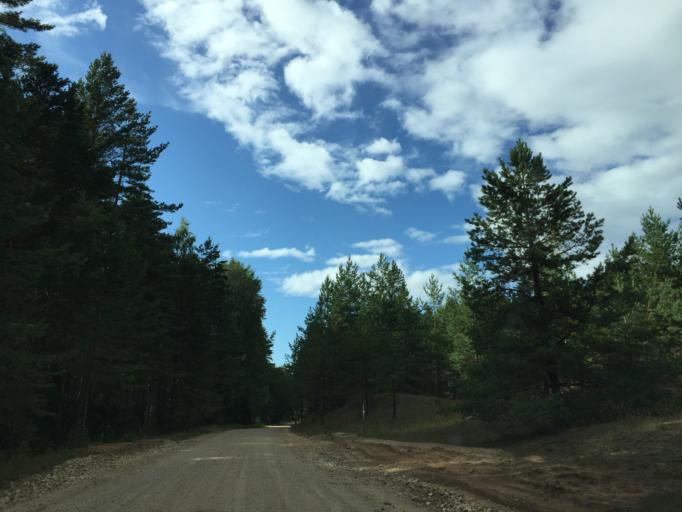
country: LV
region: Saulkrastu
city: Saulkrasti
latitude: 57.1823
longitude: 24.3762
